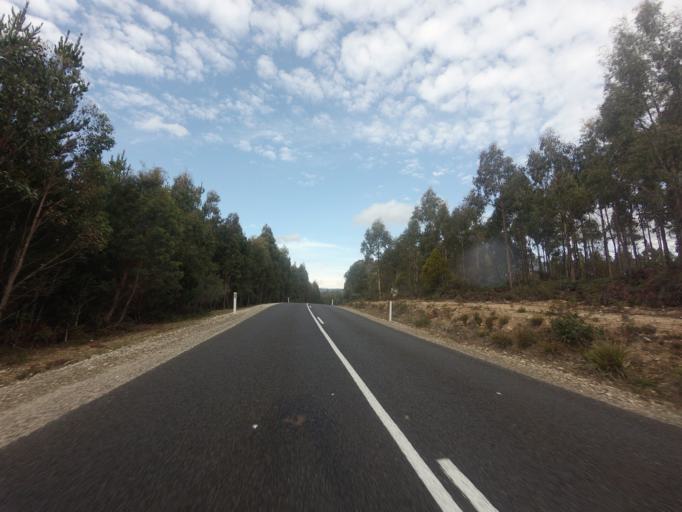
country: AU
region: Tasmania
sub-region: Meander Valley
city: Deloraine
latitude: -41.6109
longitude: 146.6852
